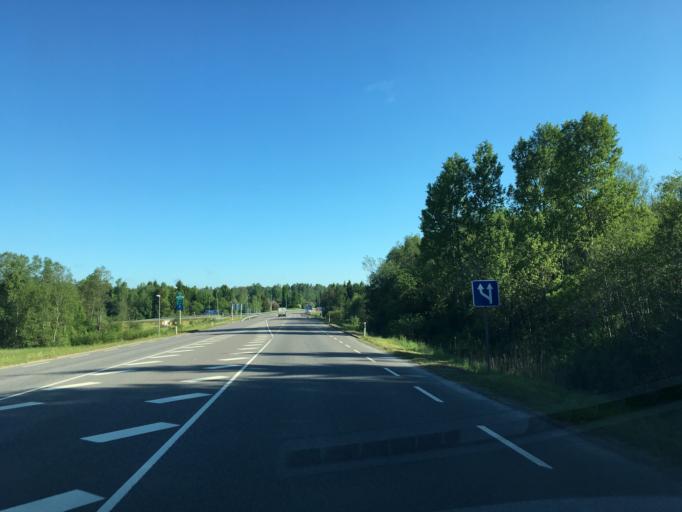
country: EE
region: Tartu
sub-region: Tartu linn
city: Tartu
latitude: 58.4568
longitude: 26.6730
